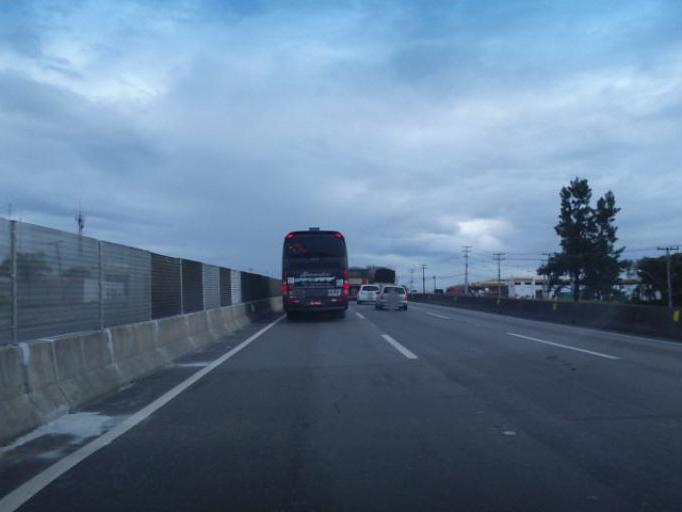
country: BR
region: Parana
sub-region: Sao Jose Dos Pinhais
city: Sao Jose dos Pinhais
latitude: -25.6083
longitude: -49.1722
